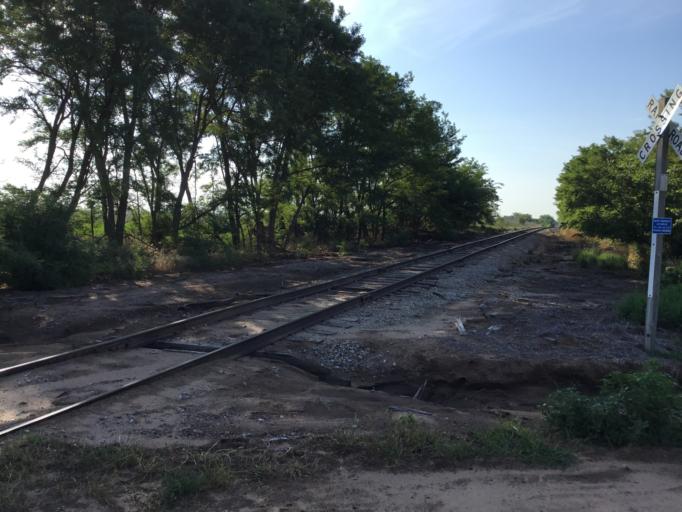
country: US
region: Kansas
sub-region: Sedgwick County
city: Cheney
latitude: 37.5068
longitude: -97.9538
